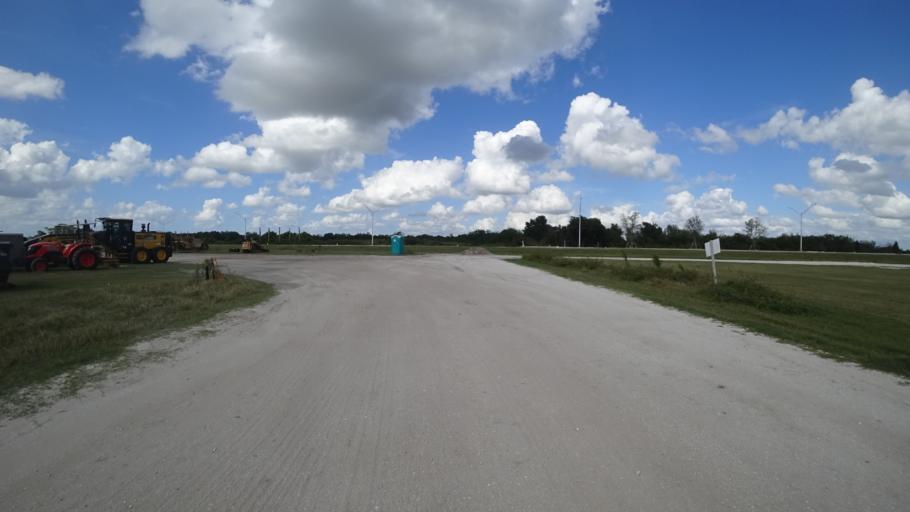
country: US
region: Florida
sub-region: Sarasota County
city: The Meadows
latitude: 27.4399
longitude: -82.3868
